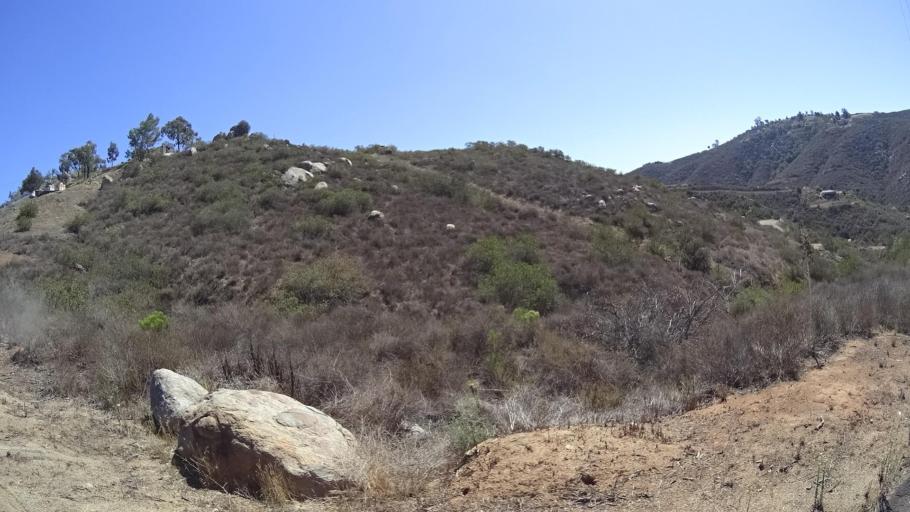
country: US
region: California
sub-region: San Diego County
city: Jamul
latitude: 32.7377
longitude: -116.8814
